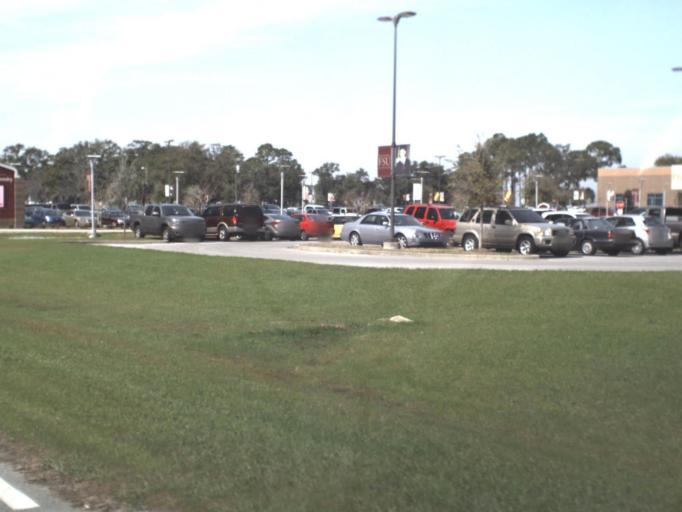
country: US
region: Florida
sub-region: Bay County
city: Pretty Bayou
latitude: 30.1883
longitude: -85.7229
